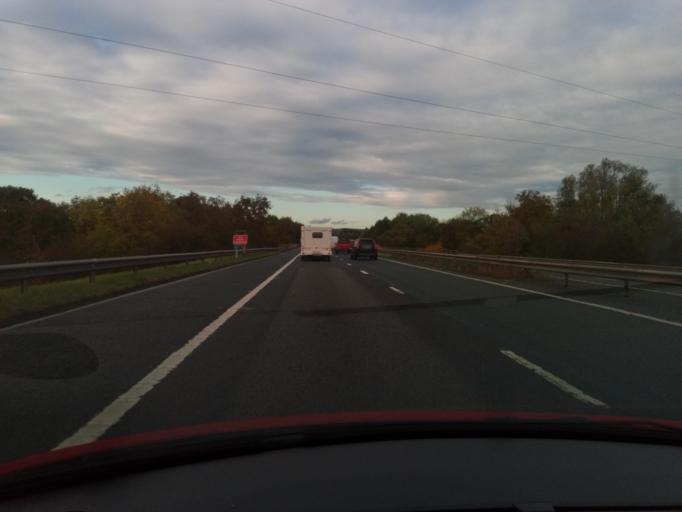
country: GB
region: England
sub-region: Darlington
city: High Coniscliffe
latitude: 54.5142
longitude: -1.6212
